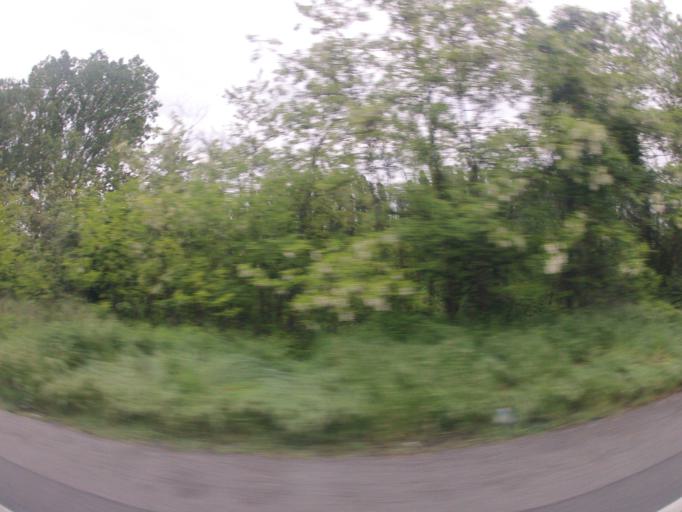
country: IT
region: Piedmont
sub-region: Provincia di Torino
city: Carignano
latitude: 44.9197
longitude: 7.6744
